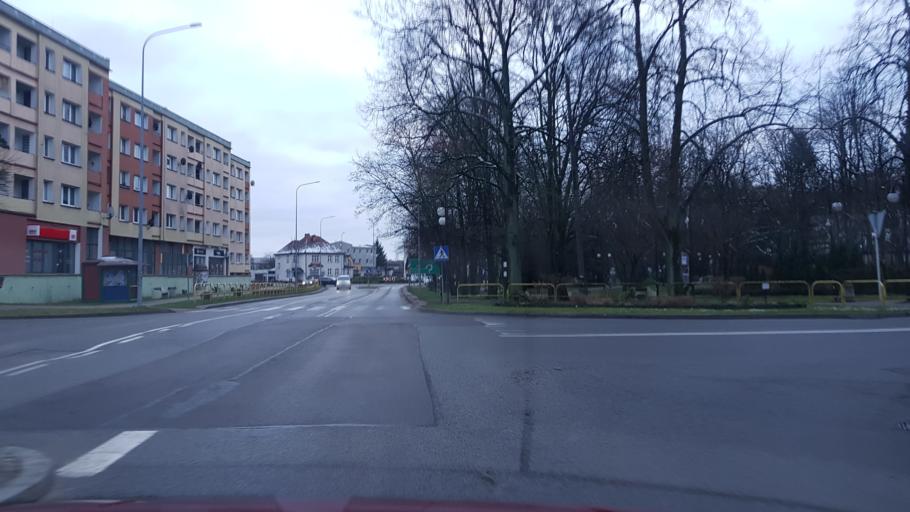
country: PL
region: Pomeranian Voivodeship
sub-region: Powiat bytowski
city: Miastko
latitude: 54.0004
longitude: 16.9755
